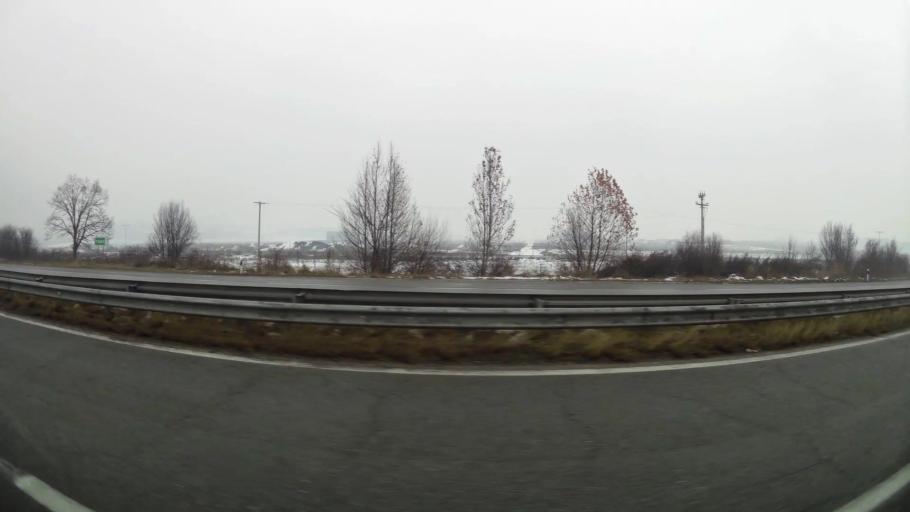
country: MK
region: Petrovec
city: Petrovec
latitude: 41.9518
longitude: 21.6307
